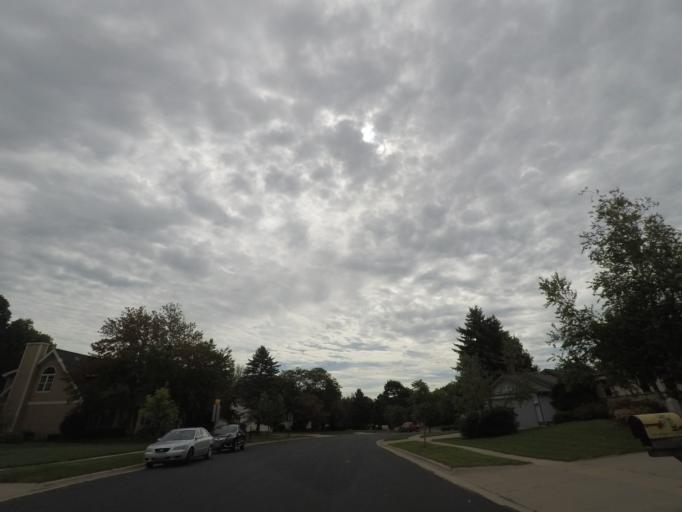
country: US
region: Wisconsin
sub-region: Dane County
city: Middleton
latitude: 43.0892
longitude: -89.4978
